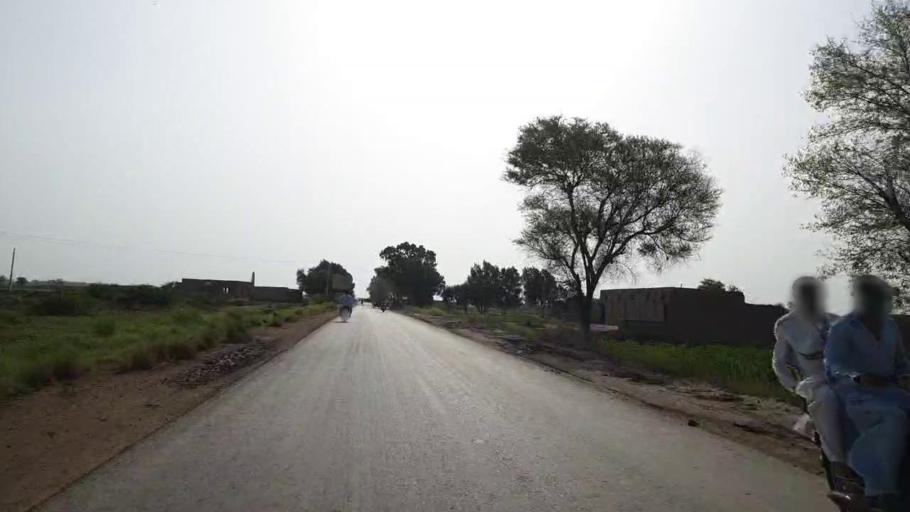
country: PK
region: Sindh
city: Nawabshah
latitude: 26.2610
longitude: 68.4885
